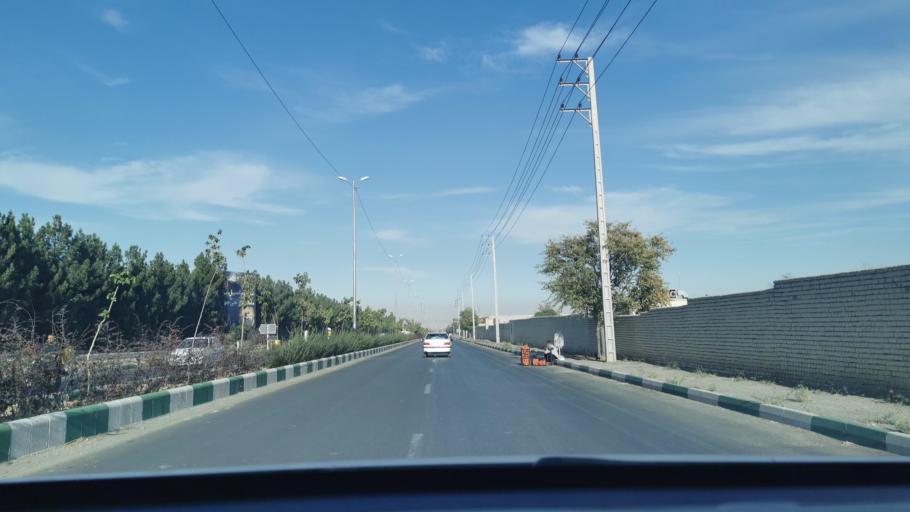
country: IR
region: Razavi Khorasan
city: Torqabeh
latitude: 36.4305
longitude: 59.4215
